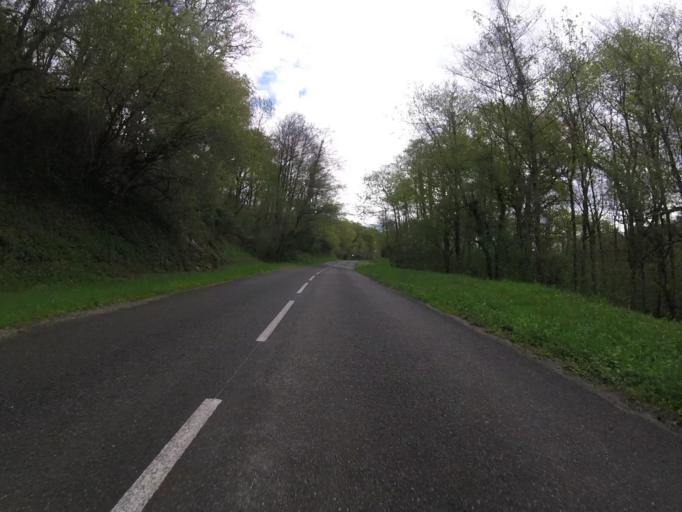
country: FR
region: Aquitaine
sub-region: Departement des Pyrenees-Atlantiques
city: Sare
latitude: 43.2870
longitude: -1.6022
